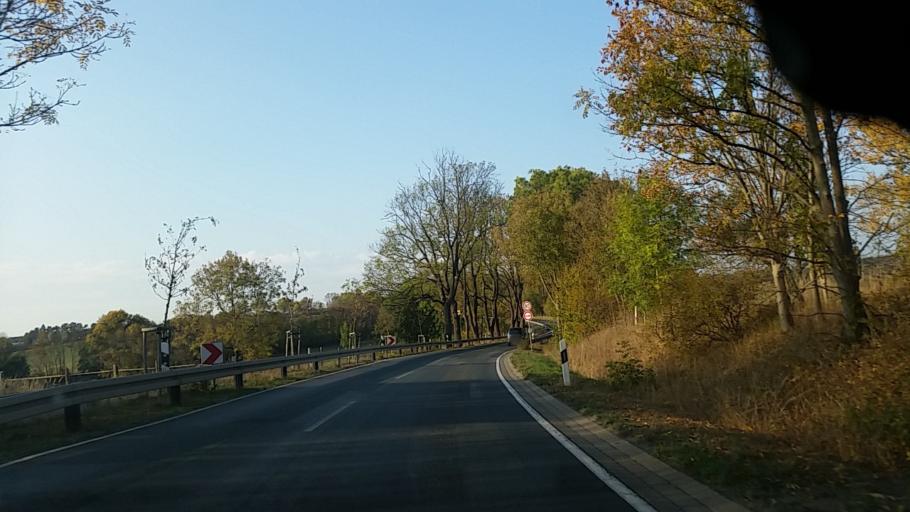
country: DE
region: Lower Saxony
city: Wolfsburg
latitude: 52.3556
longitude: 10.7648
